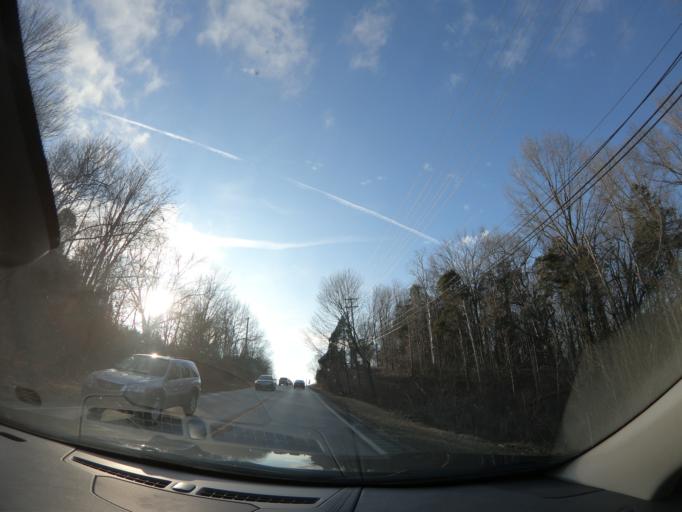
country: US
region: Kentucky
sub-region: Jefferson County
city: Jeffersontown
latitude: 38.1903
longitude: -85.4988
